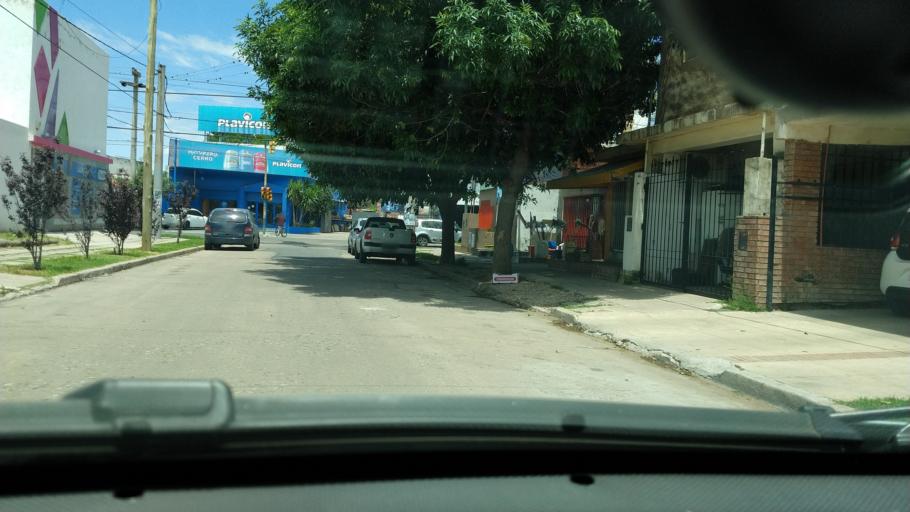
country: AR
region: Cordoba
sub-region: Departamento de Capital
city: Cordoba
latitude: -31.3613
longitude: -64.2305
